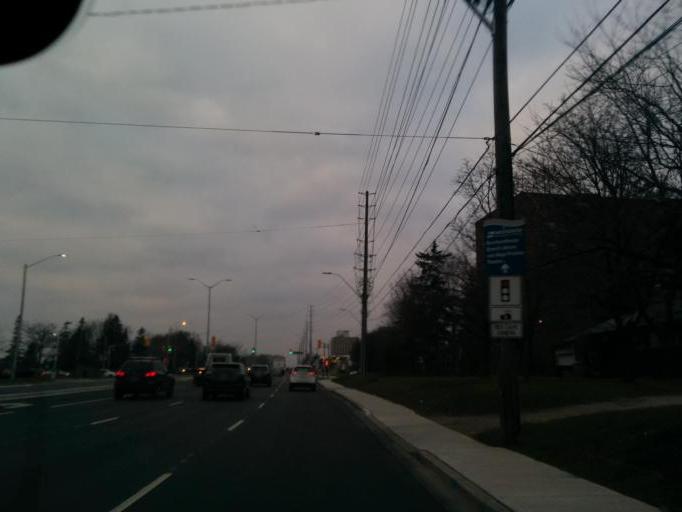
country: CA
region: Ontario
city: Etobicoke
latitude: 43.6161
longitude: -79.5934
